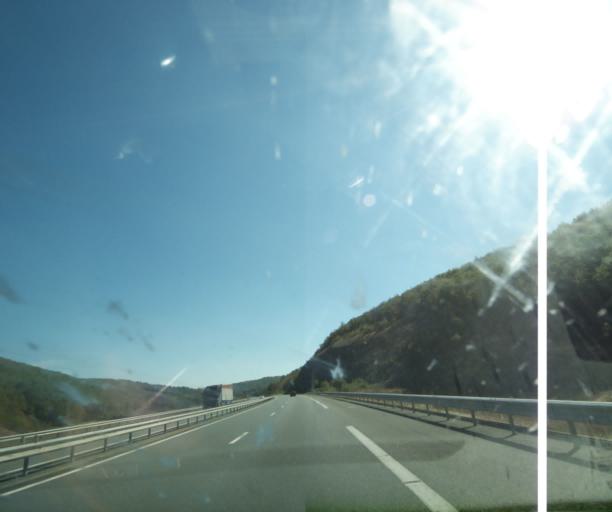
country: FR
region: Midi-Pyrenees
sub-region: Departement du Lot
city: Souillac
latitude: 44.8255
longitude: 1.4956
